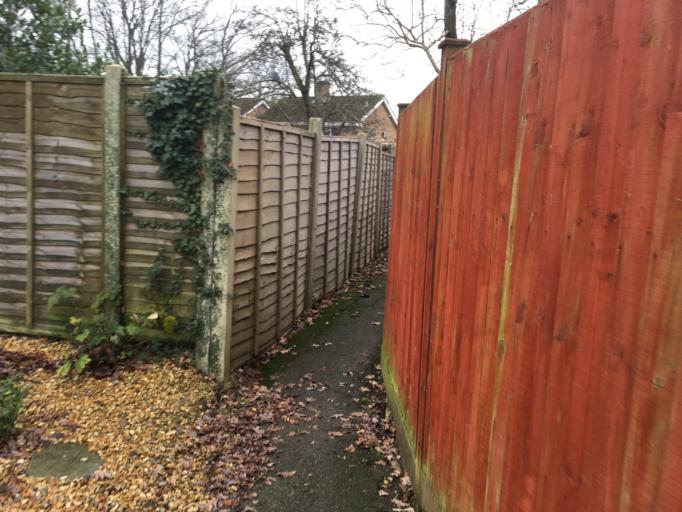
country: GB
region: England
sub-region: Hampshire
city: Colden Common
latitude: 50.9940
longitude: -1.3181
